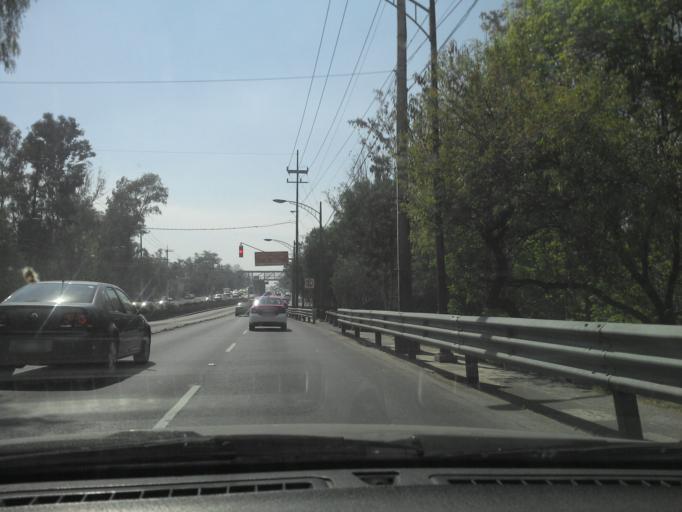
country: MX
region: Mexico City
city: Magdalena Contreras
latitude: 19.3255
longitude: -99.1889
